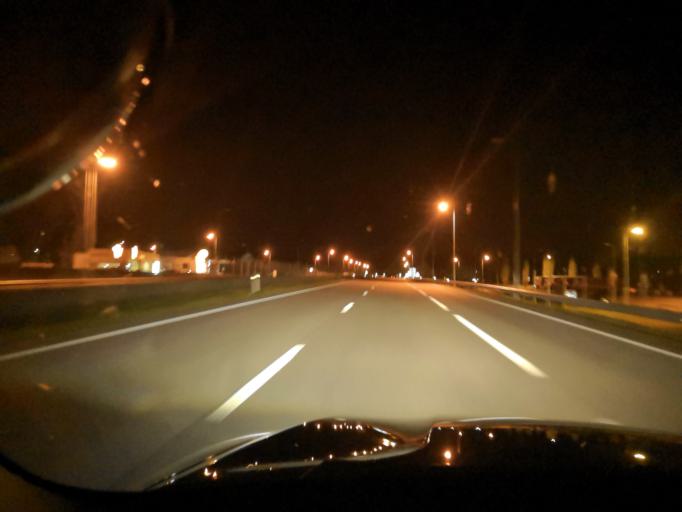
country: PT
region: Viseu
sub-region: Oliveira de Frades
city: Oliveira de Frades
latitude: 40.6864
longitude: -8.2301
